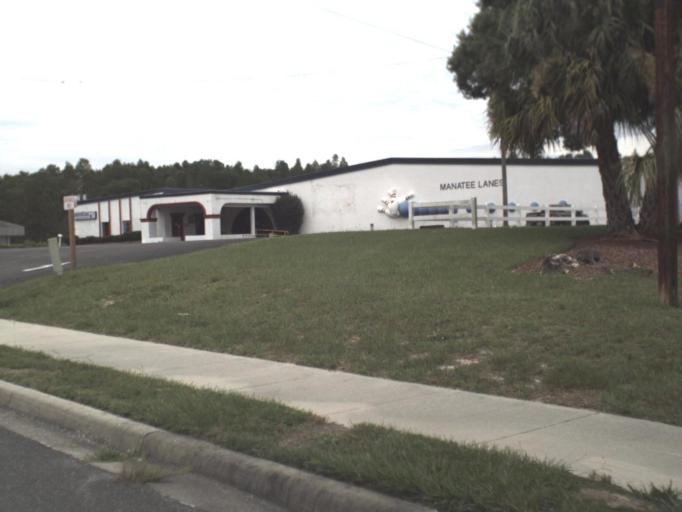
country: US
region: Florida
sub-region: Citrus County
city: Crystal River
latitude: 28.8968
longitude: -82.5623
